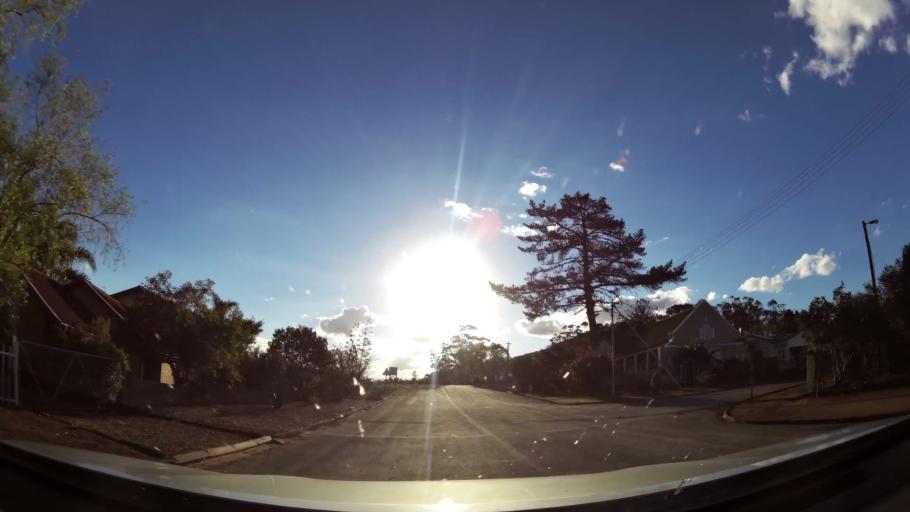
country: ZA
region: Western Cape
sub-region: Eden District Municipality
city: Riversdale
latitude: -34.0863
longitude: 20.9575
